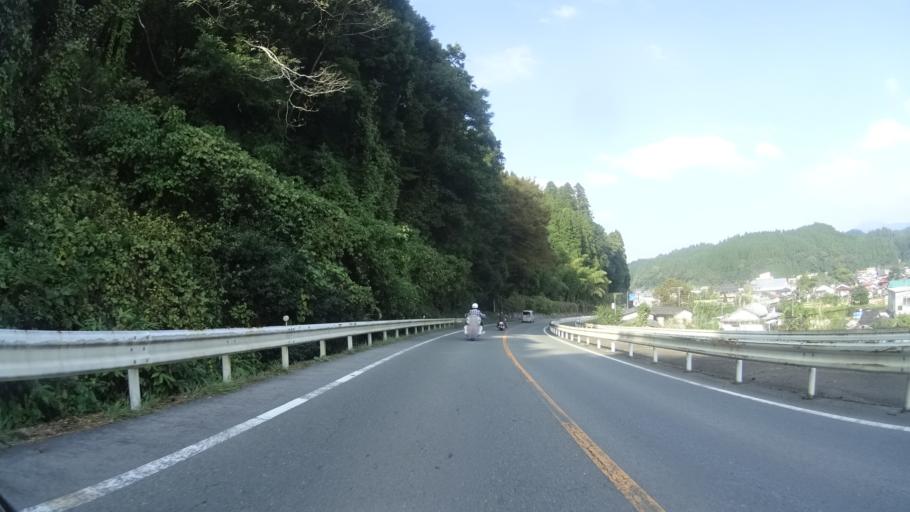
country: JP
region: Kumamoto
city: Aso
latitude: 33.0947
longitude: 131.0663
